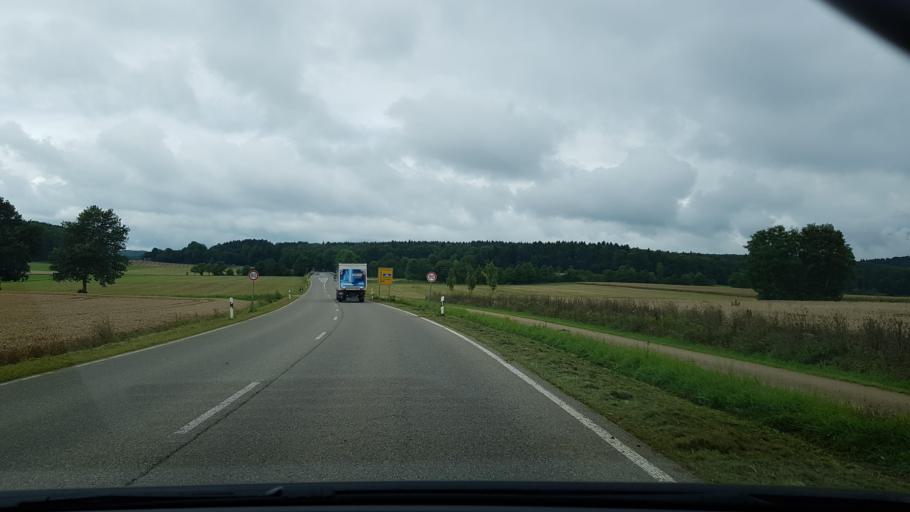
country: DE
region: Baden-Wuerttemberg
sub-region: Tuebingen Region
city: Laichingen
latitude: 48.4640
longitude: 9.6737
